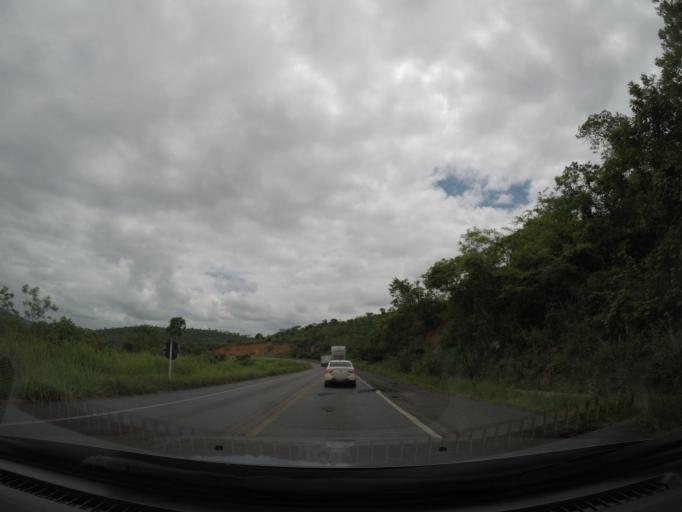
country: BR
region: Bahia
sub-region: Ruy Barbosa
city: Terra Nova
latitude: -12.4525
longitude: -40.5989
